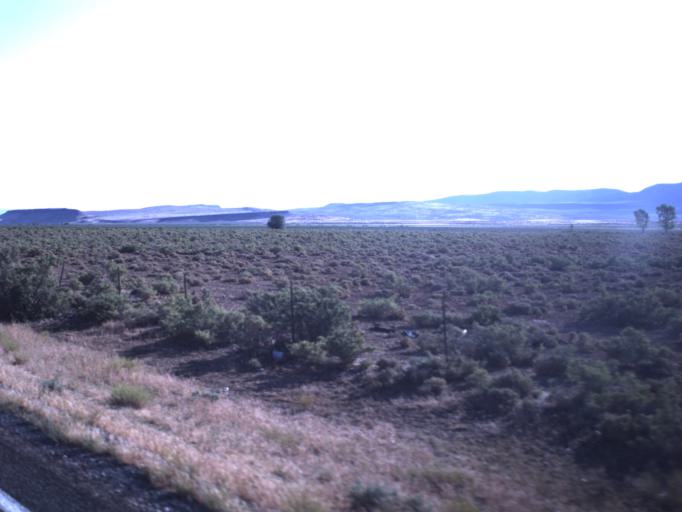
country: US
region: Utah
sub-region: Iron County
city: Enoch
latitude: 37.8067
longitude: -113.0505
